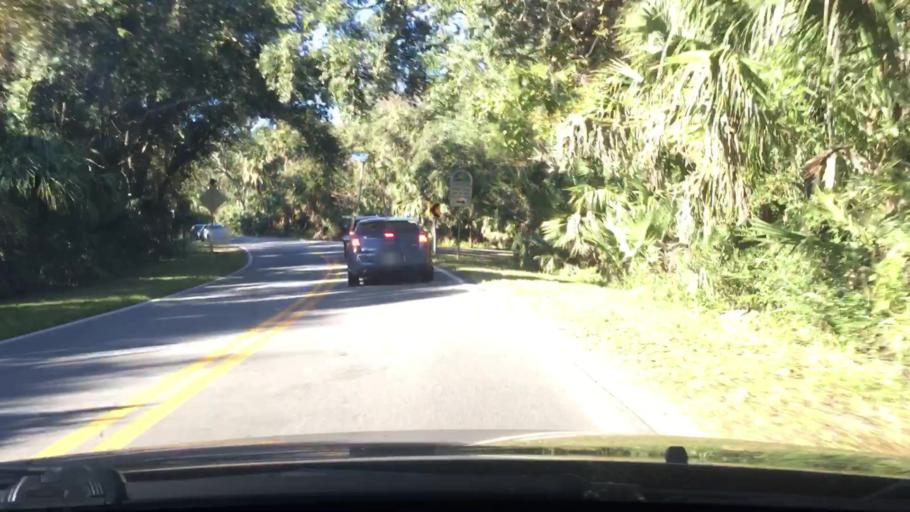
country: US
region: Florida
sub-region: Flagler County
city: Flagler Beach
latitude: 29.4027
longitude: -81.1373
